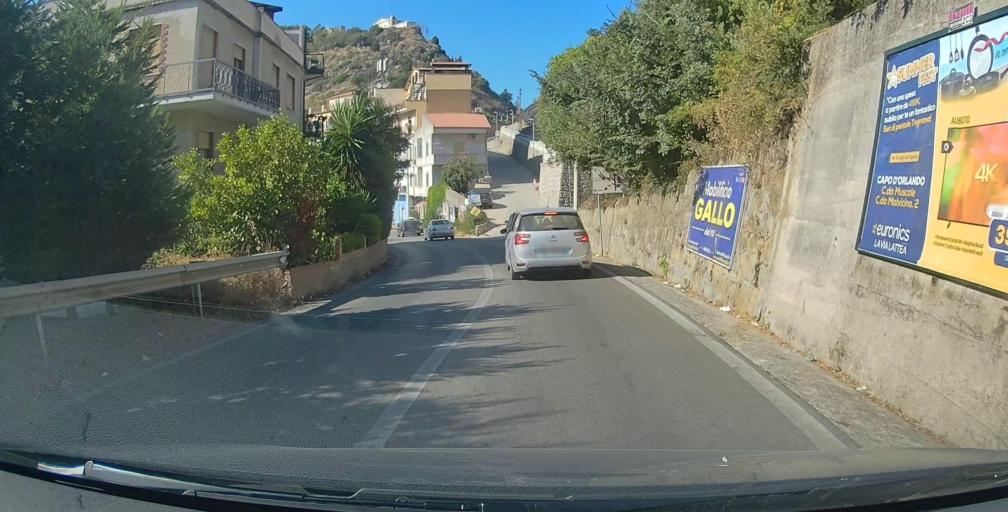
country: IT
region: Sicily
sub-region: Messina
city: Capo d'Orlando
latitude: 38.1612
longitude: 14.7489
